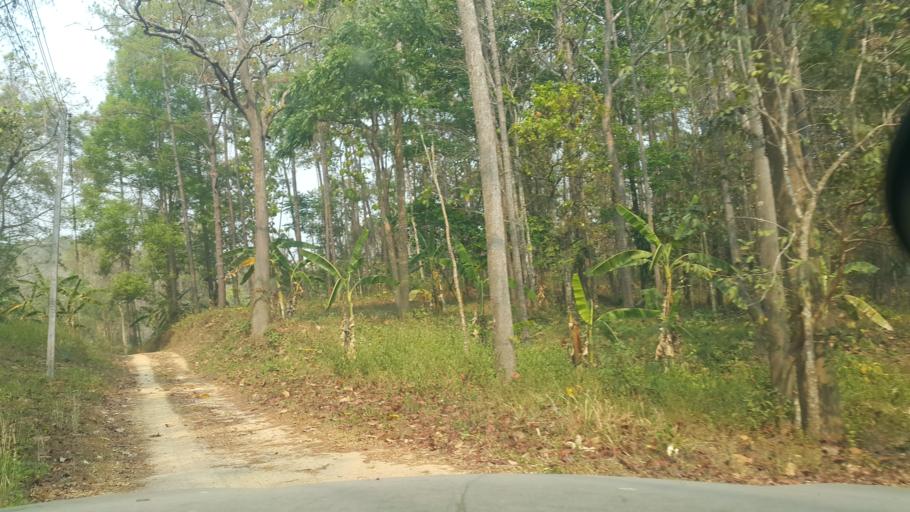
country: TH
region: Chiang Mai
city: Mae On
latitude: 18.6812
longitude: 99.2942
